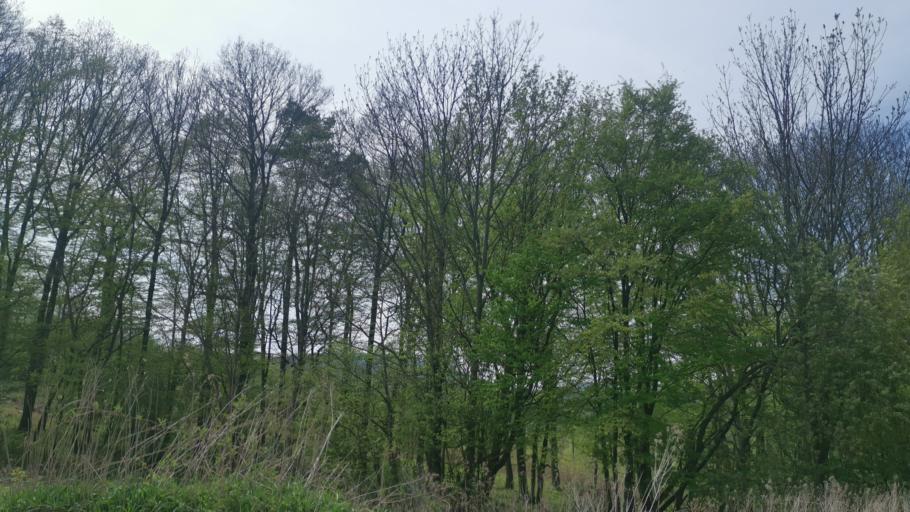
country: SK
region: Trnavsky
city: Smolenice
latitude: 48.5576
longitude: 17.4370
